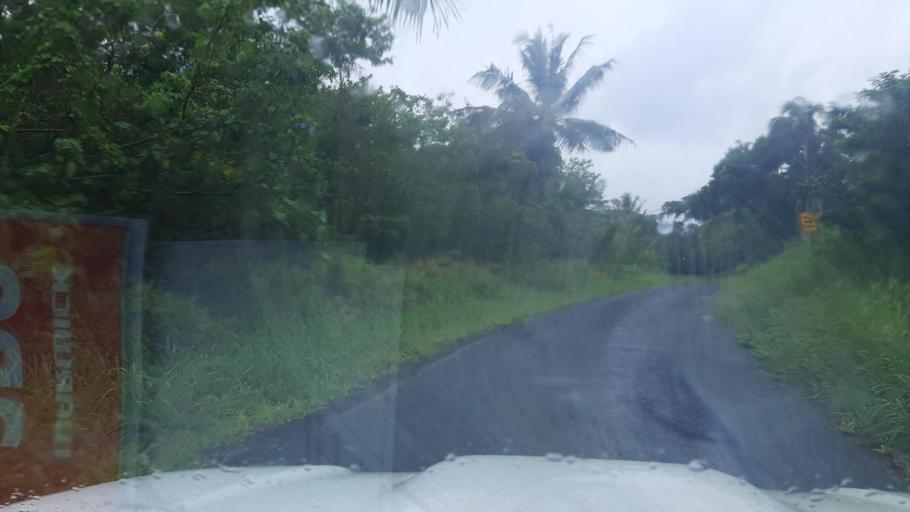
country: VU
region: Shefa
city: Port-Vila
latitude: -17.6387
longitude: 168.2115
